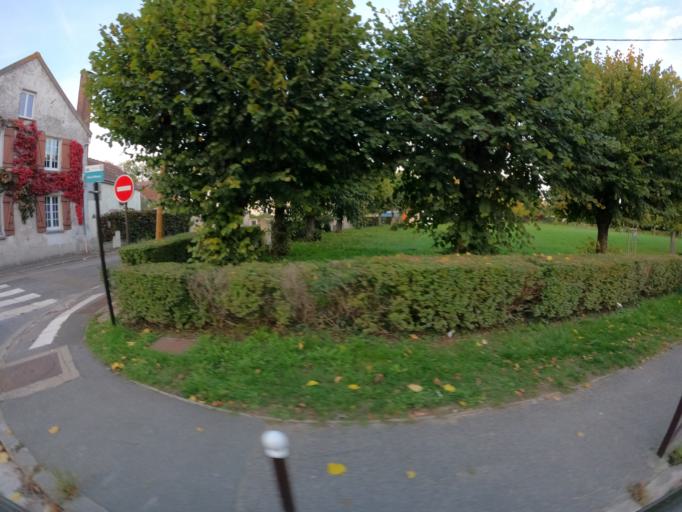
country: FR
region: Ile-de-France
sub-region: Departement de Seine-et-Marne
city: Emerainville
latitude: 48.8135
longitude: 2.6218
